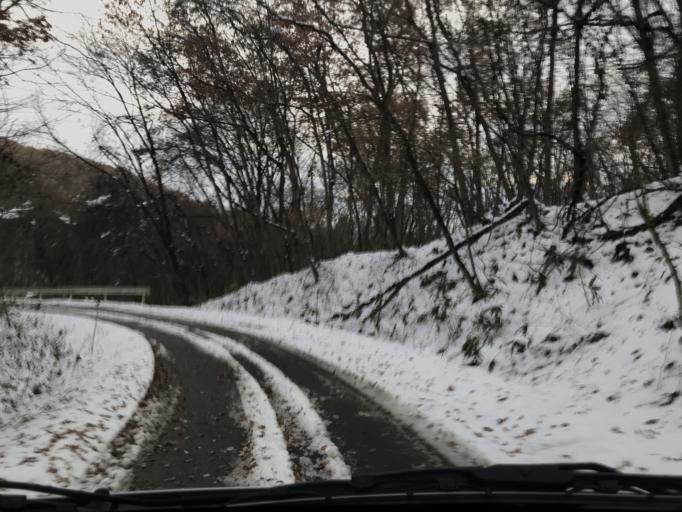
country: JP
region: Iwate
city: Mizusawa
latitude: 39.0535
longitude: 141.0579
